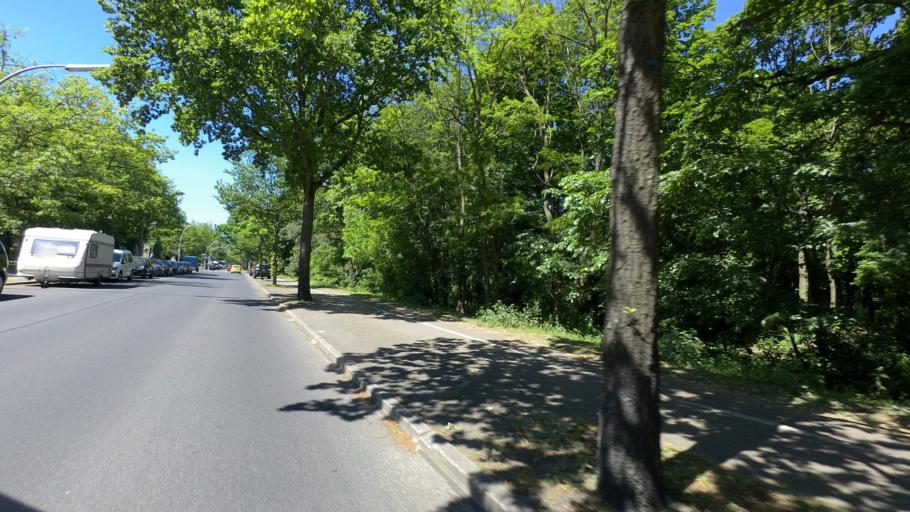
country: DE
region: Berlin
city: Charlottenburg-Nord
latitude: 52.5401
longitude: 13.2885
